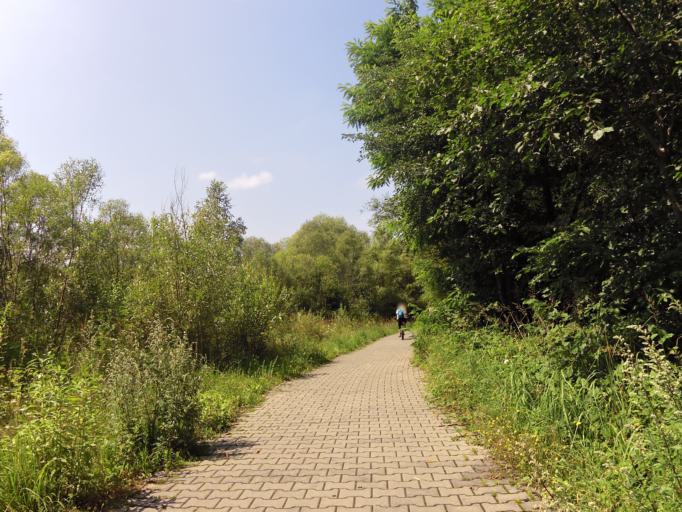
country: PL
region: Silesian Voivodeship
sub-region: Powiat zywiecki
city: Milowka
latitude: 49.5476
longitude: 19.0962
